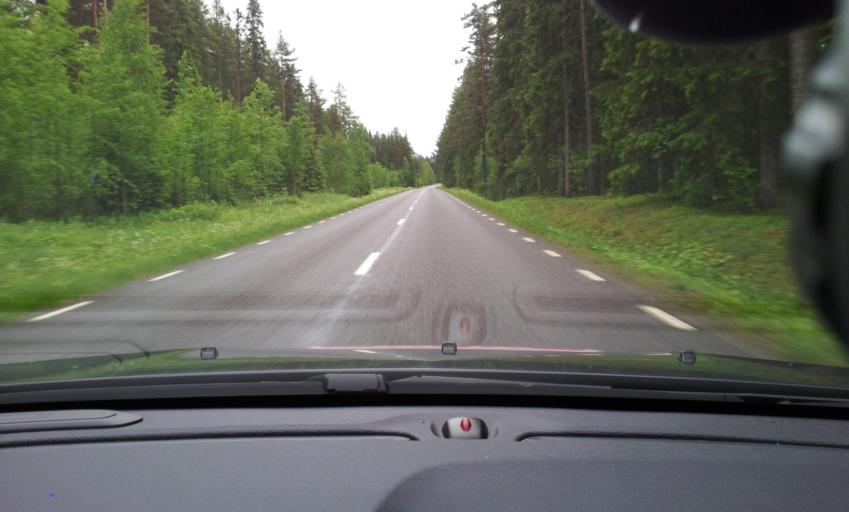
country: SE
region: Jaemtland
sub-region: Stroemsunds Kommun
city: Stroemsund
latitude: 63.4326
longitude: 15.4955
